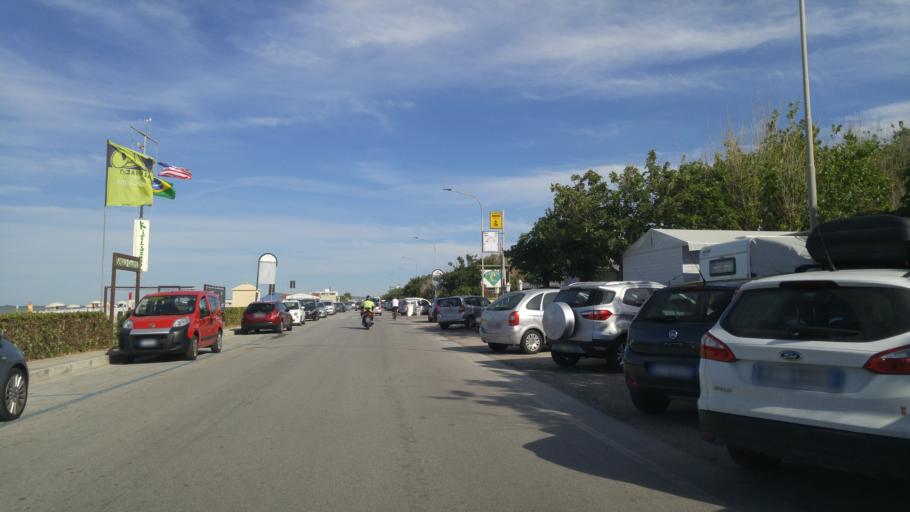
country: IT
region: The Marches
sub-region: Provincia di Ancona
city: Montignano-Marzocca
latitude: 43.6875
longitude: 13.2697
